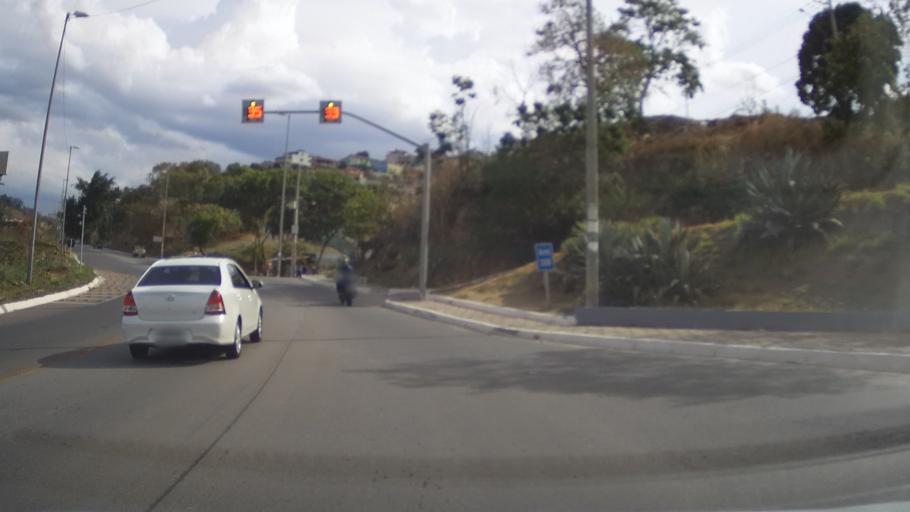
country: BR
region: Minas Gerais
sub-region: Belo Horizonte
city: Belo Horizonte
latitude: -19.8689
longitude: -43.8936
